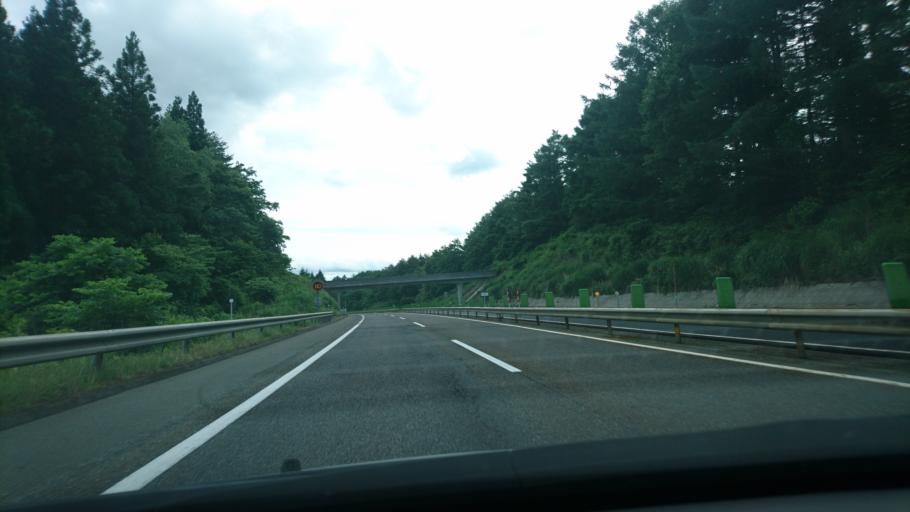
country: JP
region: Aomori
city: Hachinohe
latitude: 40.4303
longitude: 141.4417
